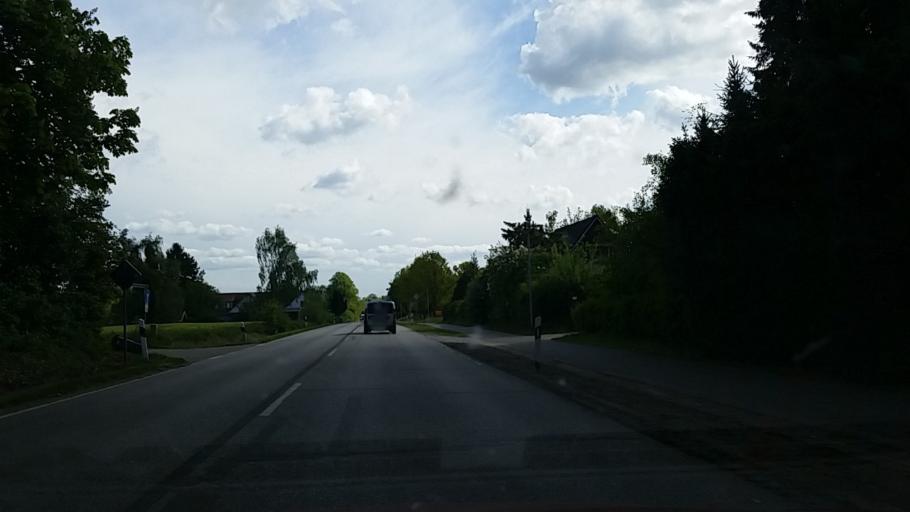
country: DE
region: Schleswig-Holstein
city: Elmenhorst
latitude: 53.7554
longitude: 10.2612
